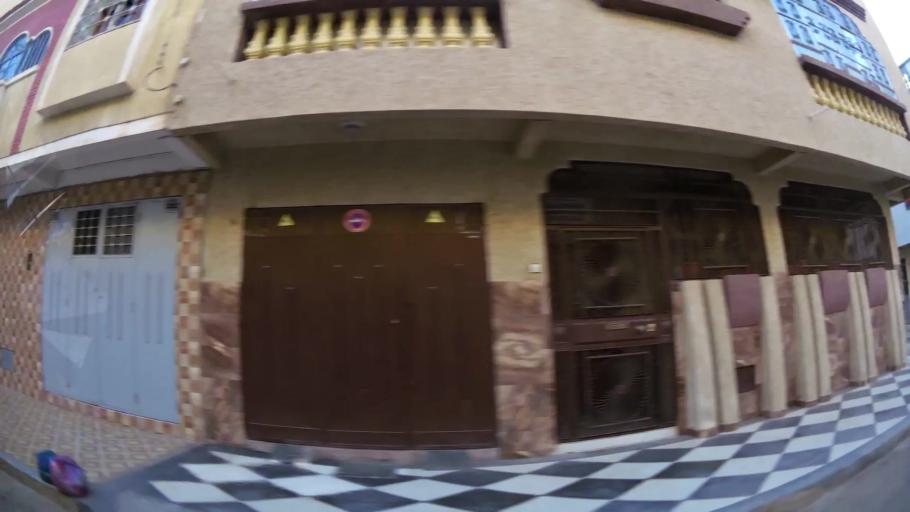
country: MA
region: Oriental
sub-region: Oujda-Angad
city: Oujda
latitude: 34.6787
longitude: -1.8901
